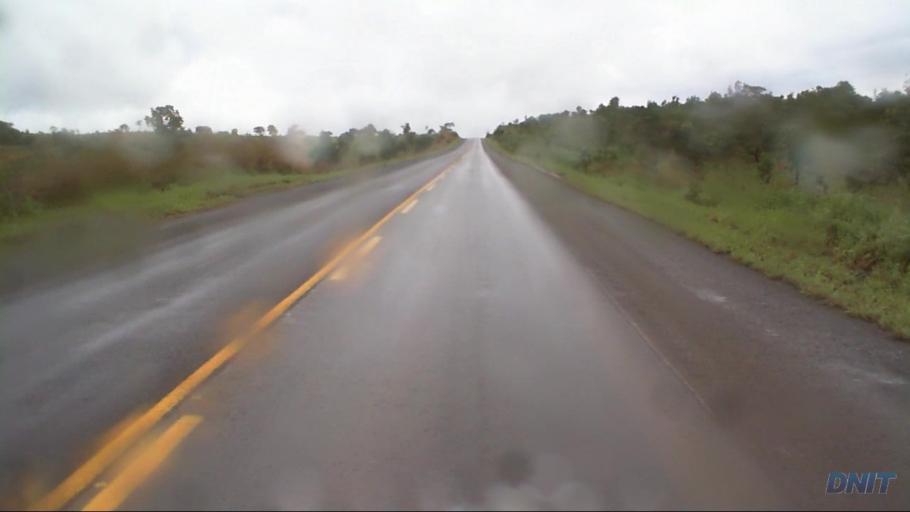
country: BR
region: Goias
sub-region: Padre Bernardo
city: Padre Bernardo
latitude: -15.2019
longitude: -48.4557
